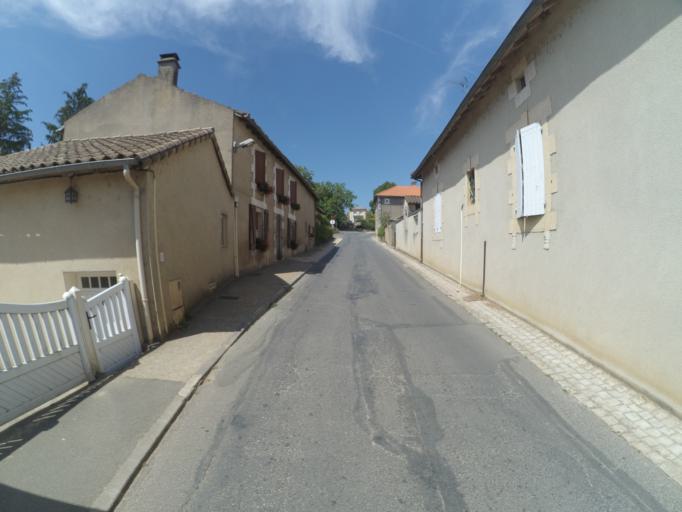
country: FR
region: Poitou-Charentes
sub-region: Departement de la Vienne
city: Vivonne
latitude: 46.4184
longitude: 0.3110
